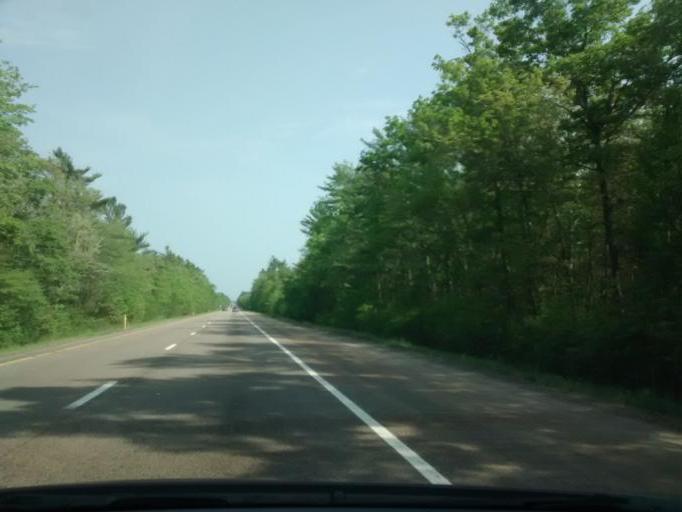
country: US
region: Massachusetts
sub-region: Plymouth County
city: Carver
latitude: 41.8355
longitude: -70.8224
